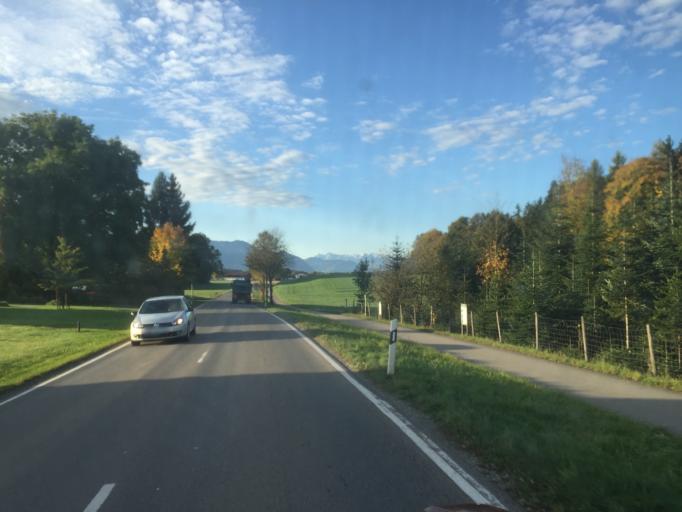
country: DE
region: Bavaria
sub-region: Upper Bavaria
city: Chieming
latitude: 47.9070
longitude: 12.5549
